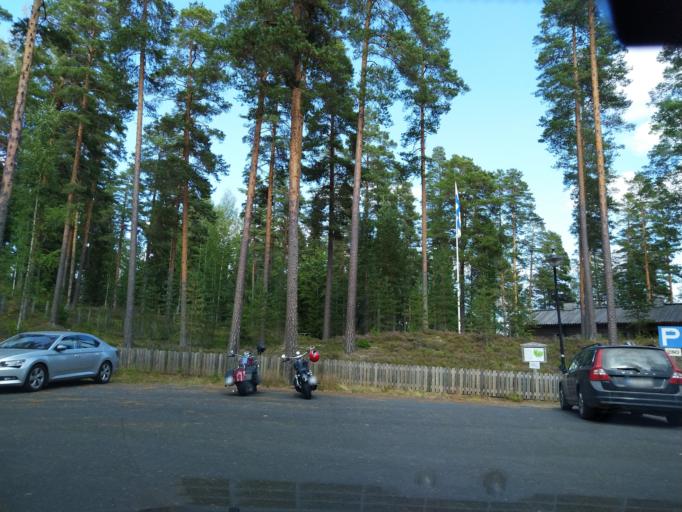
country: FI
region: Uusimaa
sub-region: Helsinki
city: Karkkila
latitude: 60.7170
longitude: 24.2120
